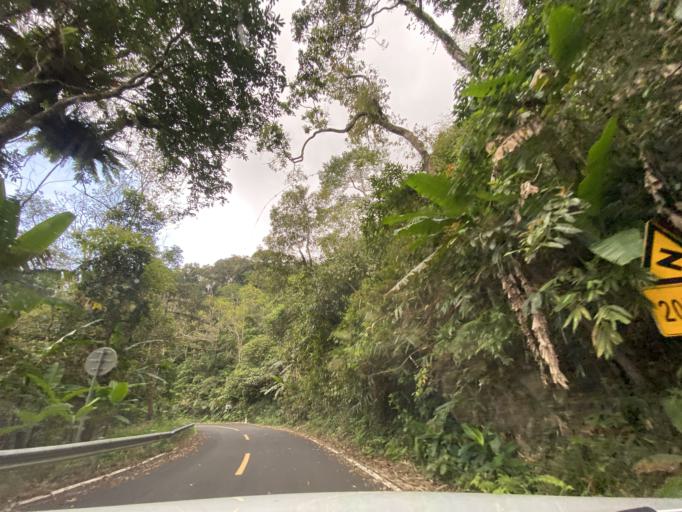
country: CN
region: Hainan
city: Diaoluoshan
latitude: 18.7138
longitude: 109.8797
